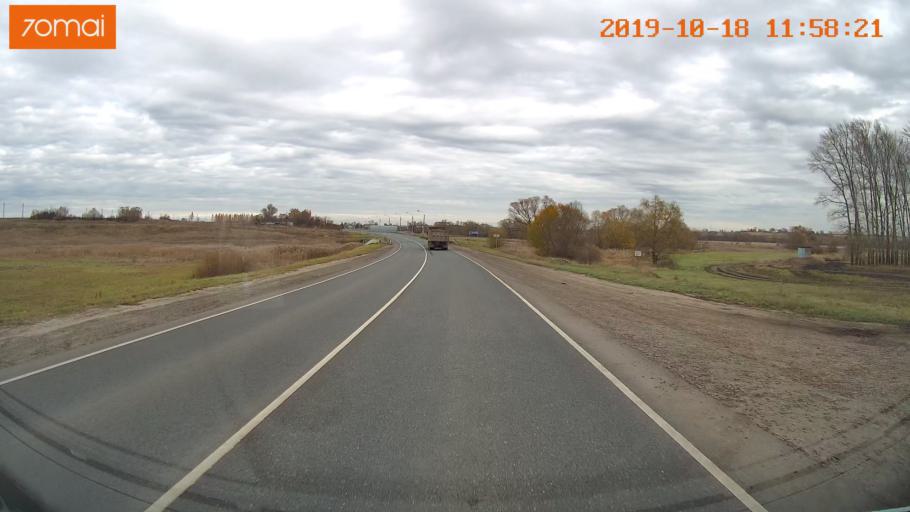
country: RU
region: Rjazan
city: Mikhaylov
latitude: 54.2708
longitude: 39.1664
